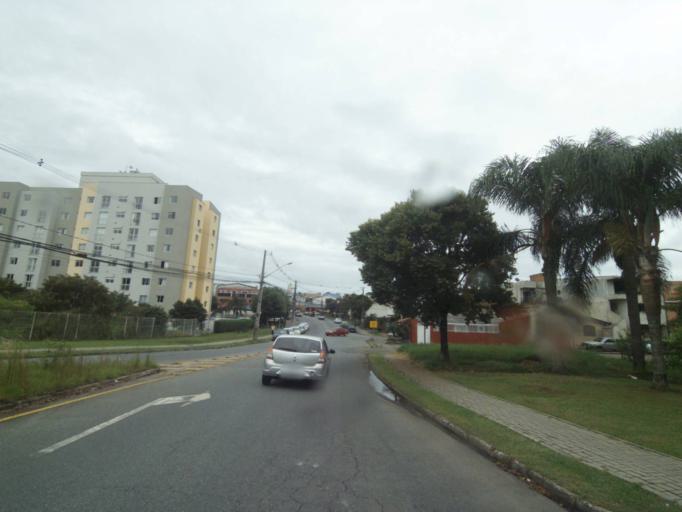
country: BR
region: Parana
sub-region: Curitiba
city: Curitiba
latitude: -25.4600
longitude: -49.3393
